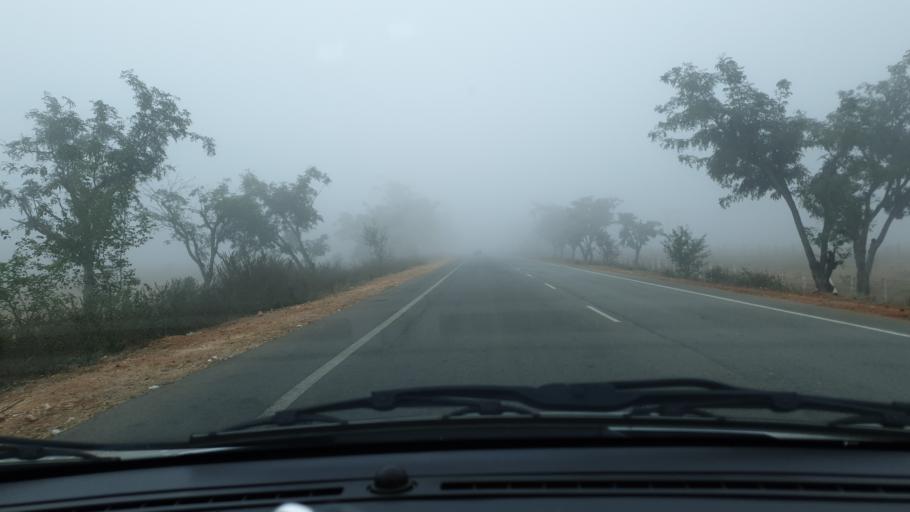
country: IN
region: Telangana
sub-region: Mahbubnagar
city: Nagar Karnul
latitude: 16.6549
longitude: 78.5760
